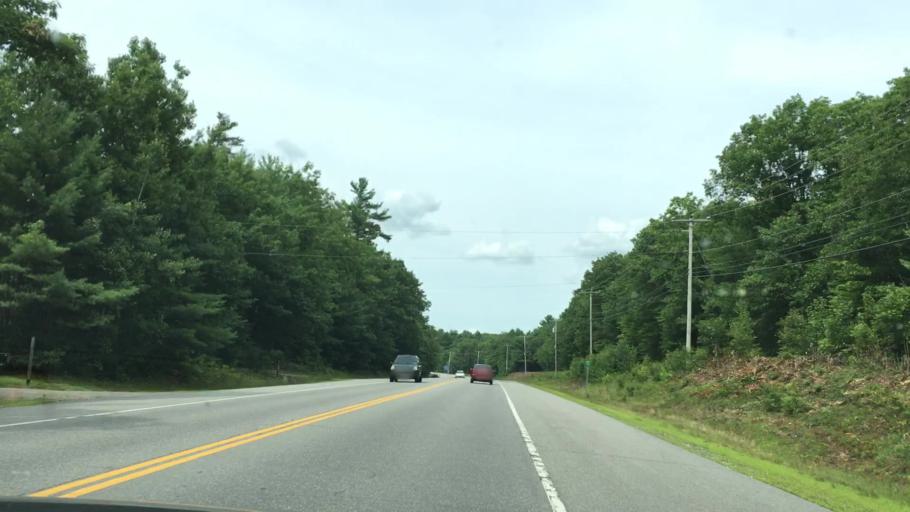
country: US
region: New Hampshire
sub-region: Cheshire County
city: Rindge
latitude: 42.7723
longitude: -72.0334
